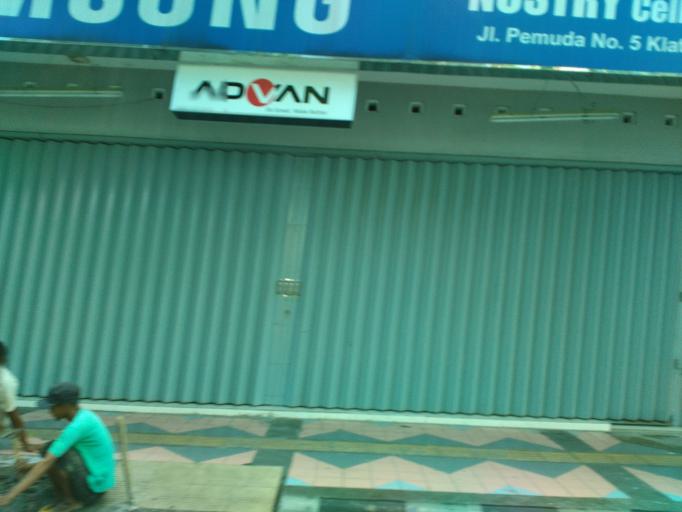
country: ID
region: Central Java
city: Klaten
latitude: -7.7024
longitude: 110.6032
